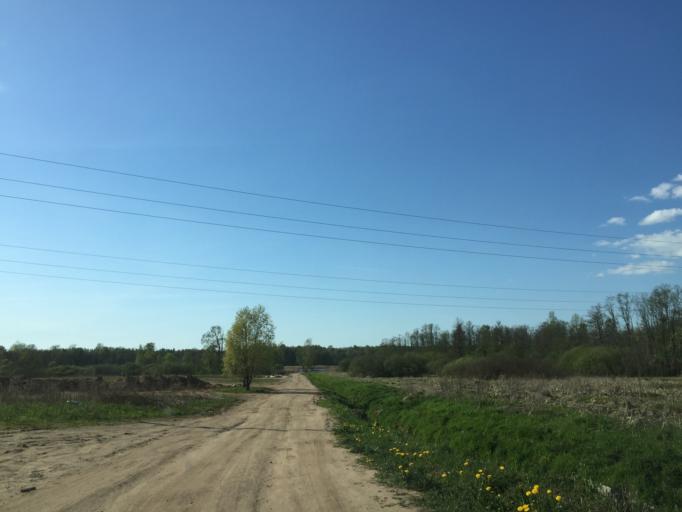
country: LV
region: Limbazu Rajons
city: Limbazi
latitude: 57.5177
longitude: 24.7071
